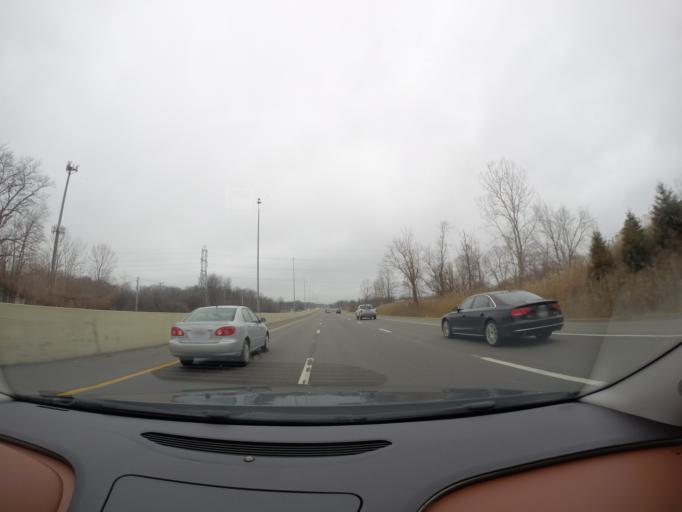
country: US
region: Ohio
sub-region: Summit County
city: Fairlawn
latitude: 41.1192
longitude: -81.6282
